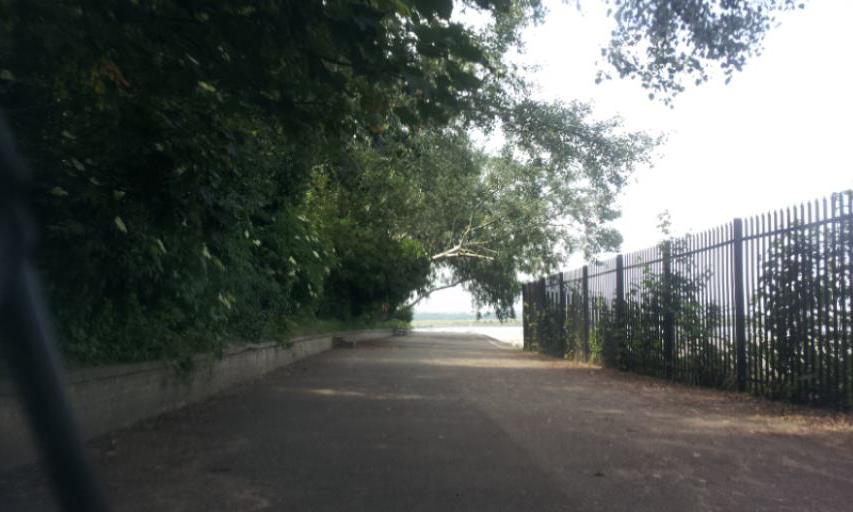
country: GB
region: England
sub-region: Kent
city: Gillingham
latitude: 51.3934
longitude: 0.5682
